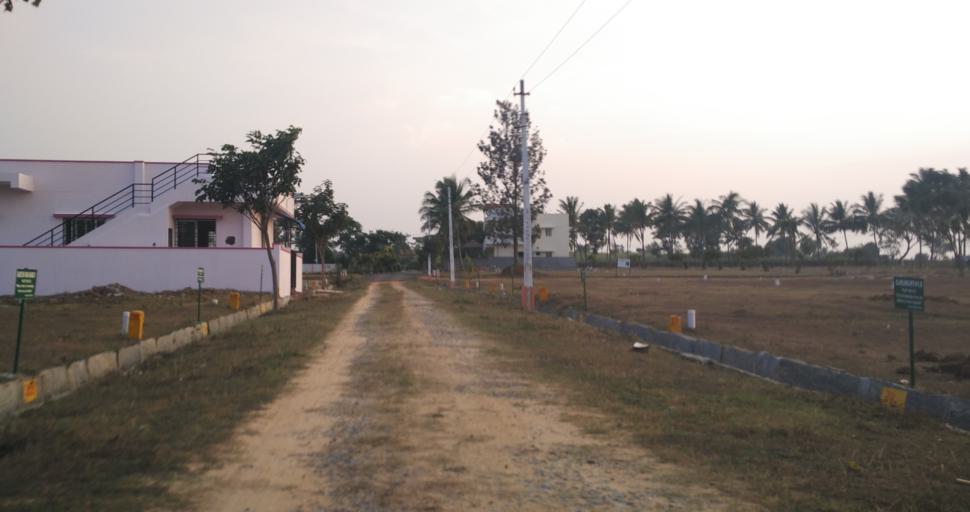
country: IN
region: Tamil Nadu
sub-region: Krishnagiri
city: Hosur
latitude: 12.6699
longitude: 77.8270
